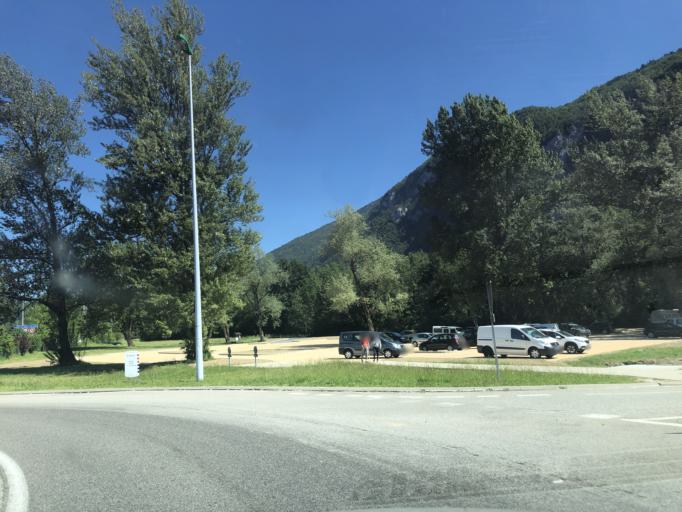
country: FR
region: Rhone-Alpes
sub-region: Departement de la Savoie
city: Novalaise
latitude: 45.5745
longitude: 5.8007
